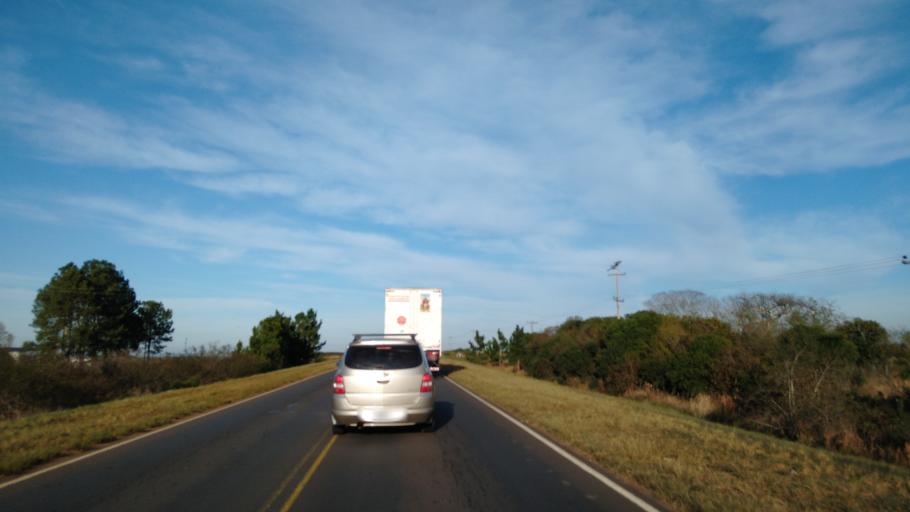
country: AR
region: Corrientes
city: La Cruz
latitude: -29.2086
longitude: -56.6995
